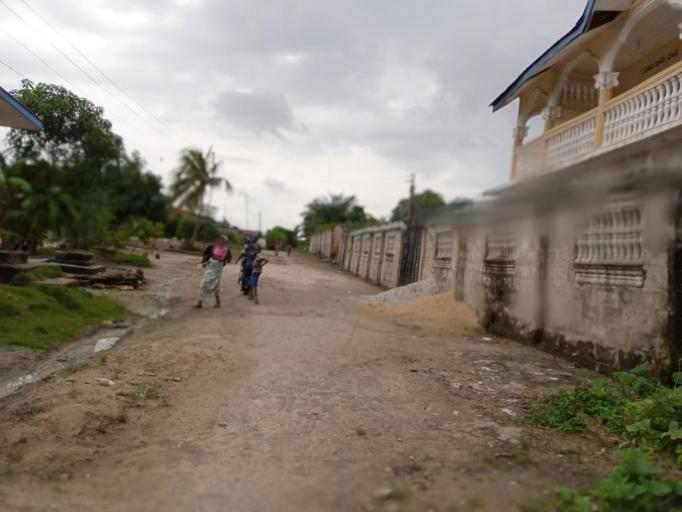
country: SL
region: Eastern Province
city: Kenema
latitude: 7.8581
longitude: -11.1986
